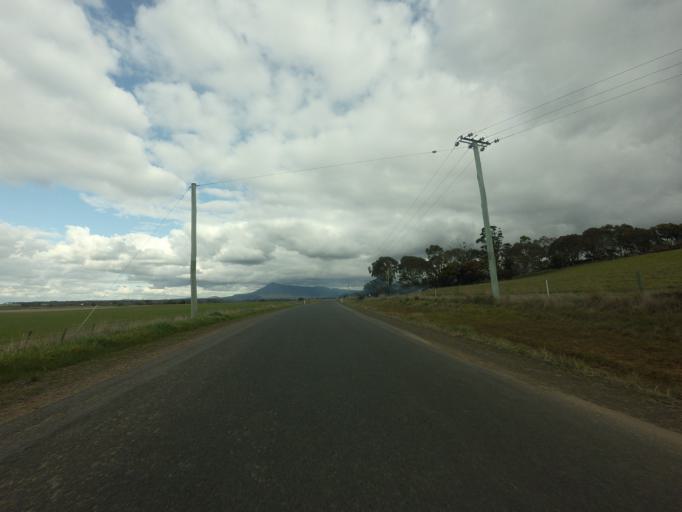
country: AU
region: Tasmania
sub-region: Northern Midlands
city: Longford
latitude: -41.7776
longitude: 147.0962
